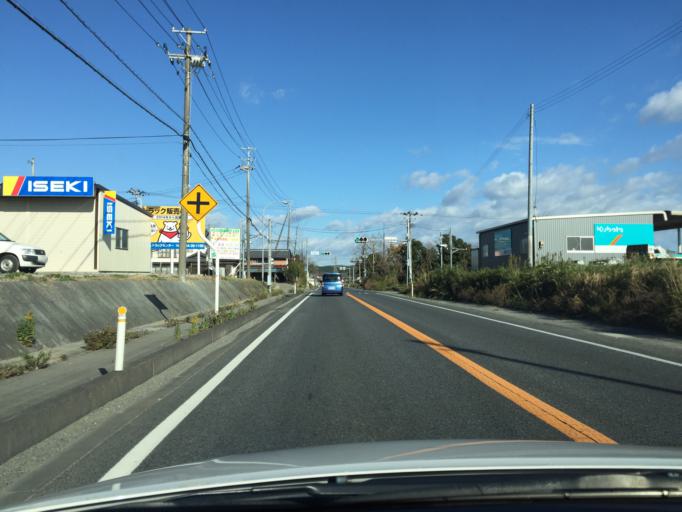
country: JP
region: Fukushima
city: Namie
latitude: 37.2577
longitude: 140.9981
